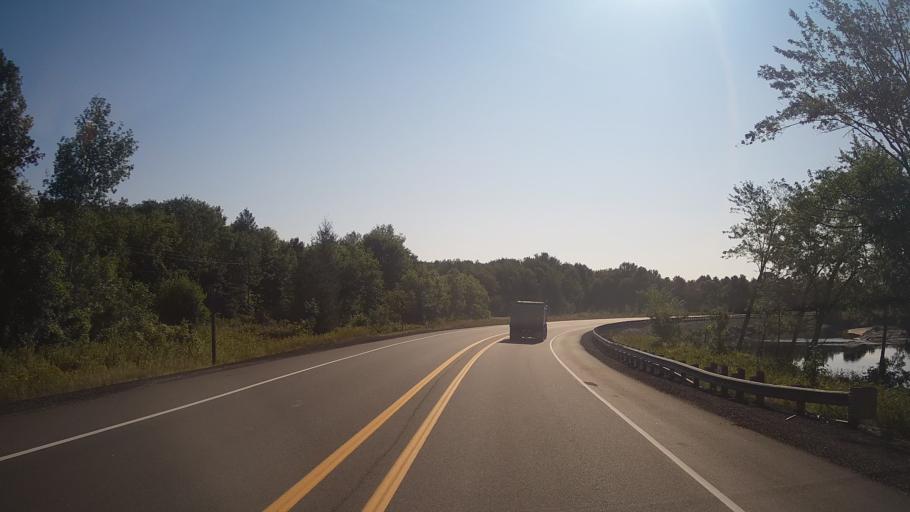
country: CA
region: Ontario
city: Elliot Lake
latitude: 46.2078
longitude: -83.0294
